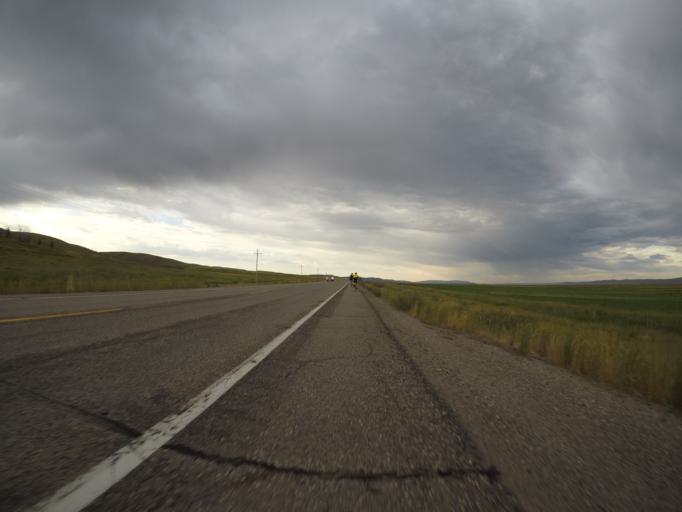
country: US
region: Utah
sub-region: Rich County
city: Randolph
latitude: 41.9623
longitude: -110.9480
